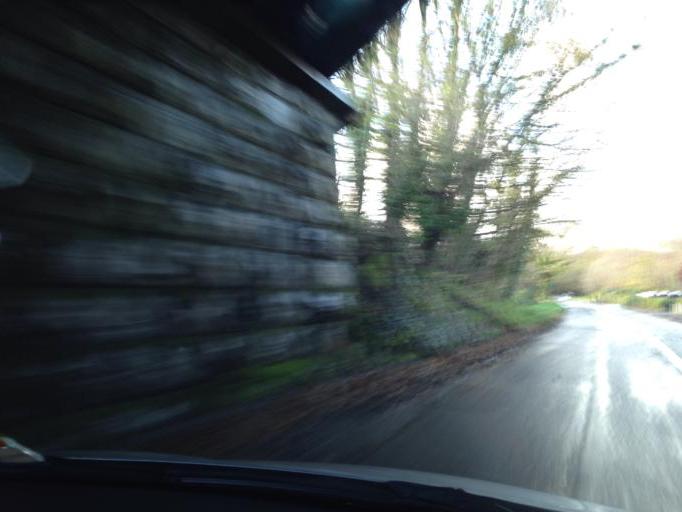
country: IE
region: Connaught
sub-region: County Galway
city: Gaillimh
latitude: 53.2725
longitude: -8.9861
